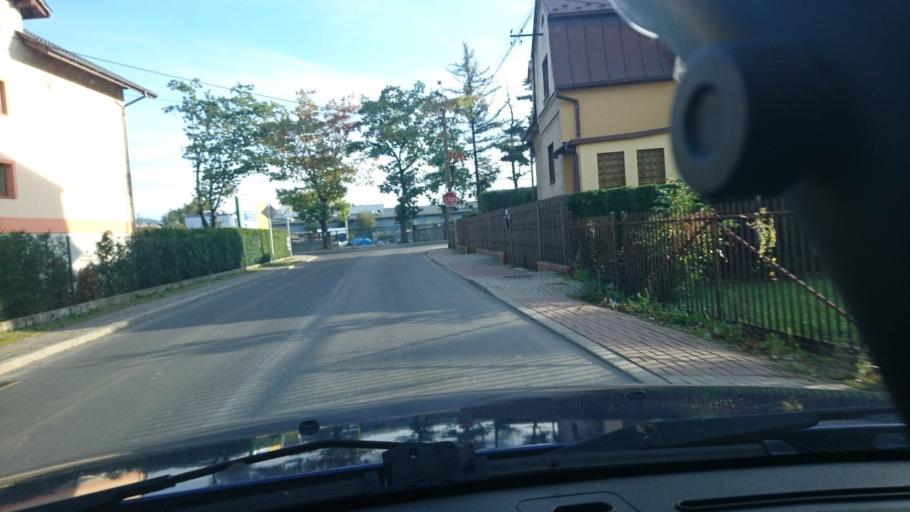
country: PL
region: Silesian Voivodeship
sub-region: Bielsko-Biala
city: Bielsko-Biala
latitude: 49.8411
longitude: 19.0558
